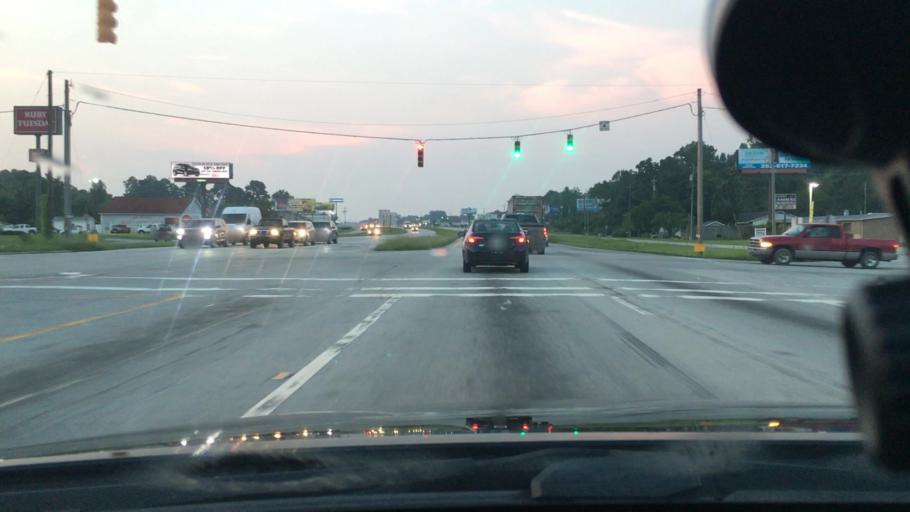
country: US
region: North Carolina
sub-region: Craven County
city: James City
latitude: 35.0820
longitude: -77.0313
